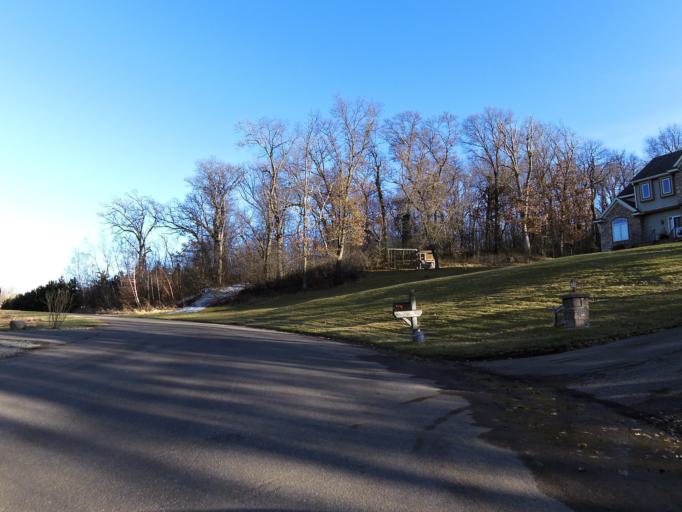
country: US
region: Minnesota
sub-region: Washington County
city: Lakeland
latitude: 44.9714
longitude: -92.8105
